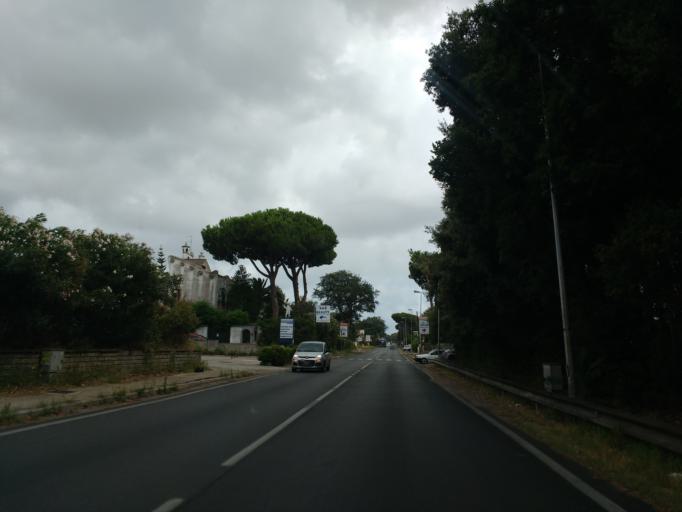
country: IT
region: Latium
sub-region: Citta metropolitana di Roma Capitale
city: Lavinio
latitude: 41.4879
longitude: 12.5986
